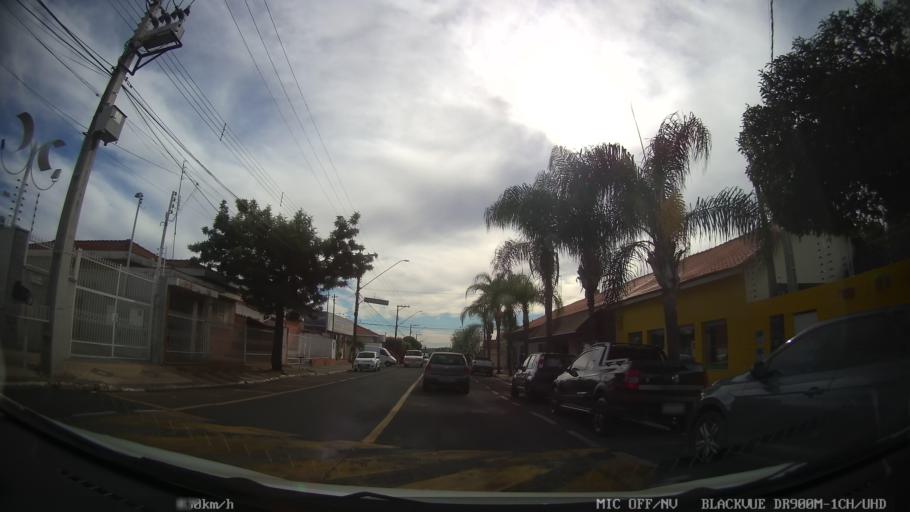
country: BR
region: Sao Paulo
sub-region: Catanduva
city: Catanduva
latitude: -21.1411
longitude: -48.9815
